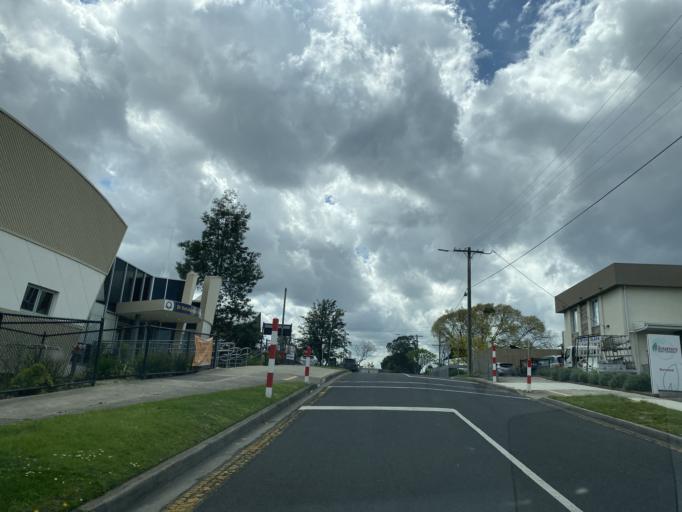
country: AU
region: Victoria
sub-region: Whitehorse
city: Burwood
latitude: -37.8524
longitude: 145.1263
